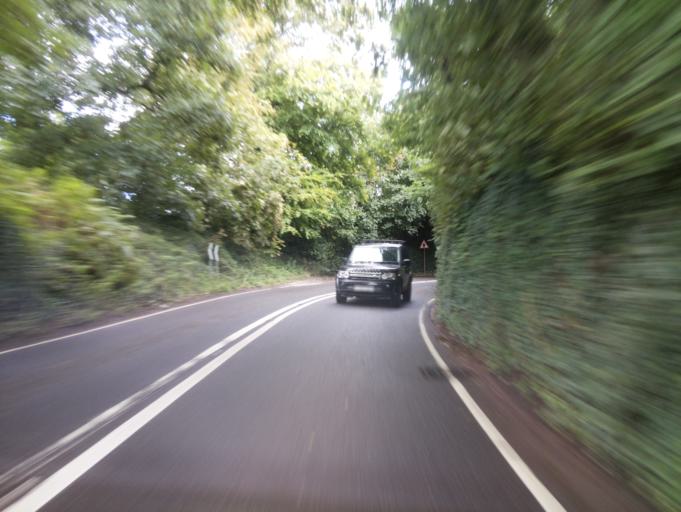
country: GB
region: England
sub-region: Devon
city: Modbury
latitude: 50.3503
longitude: -3.9220
